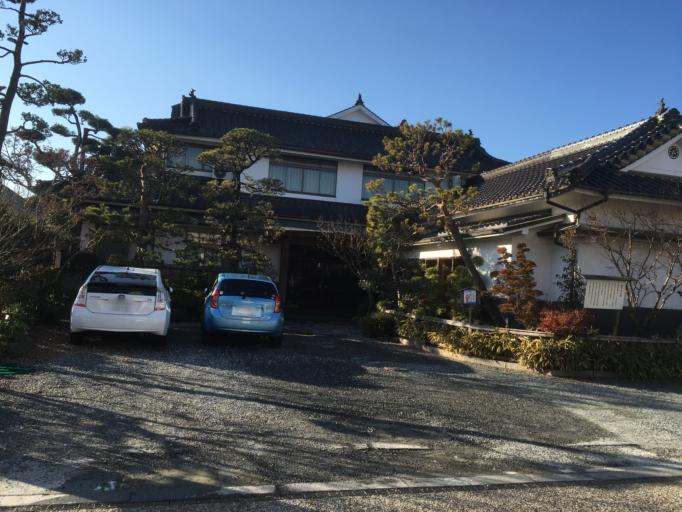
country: JP
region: Oita
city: Hita
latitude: 33.3281
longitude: 130.9374
